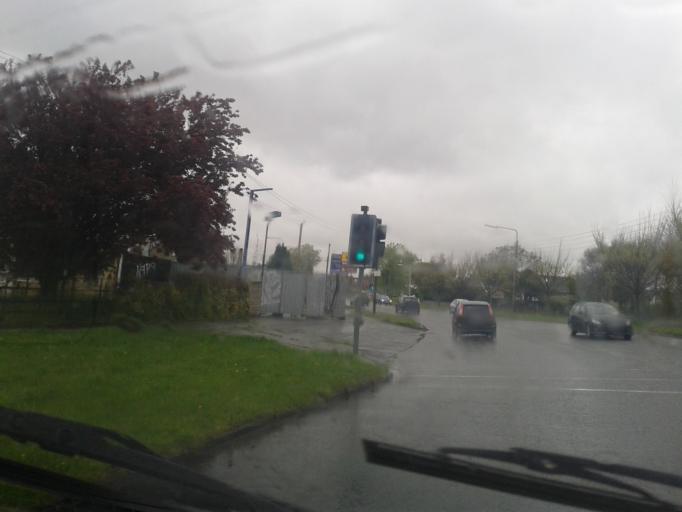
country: IE
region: Leinster
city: Templeogue
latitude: 53.3036
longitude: -6.3221
